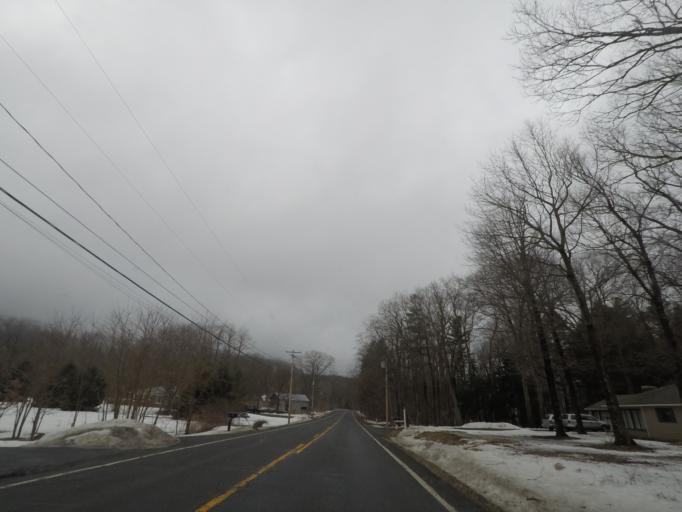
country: US
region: New York
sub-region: Albany County
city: Altamont
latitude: 42.6587
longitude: -73.9938
